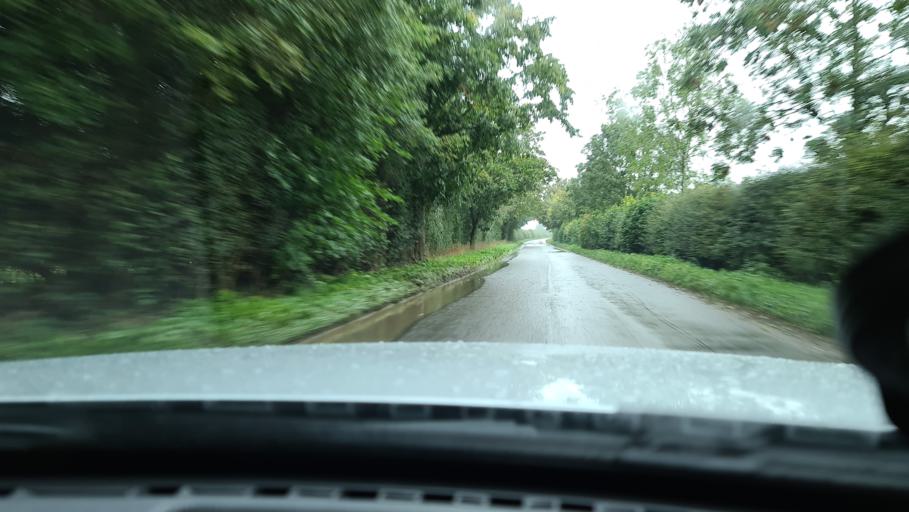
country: GB
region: England
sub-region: Oxfordshire
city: Woodstock
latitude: 51.8960
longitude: -1.3791
